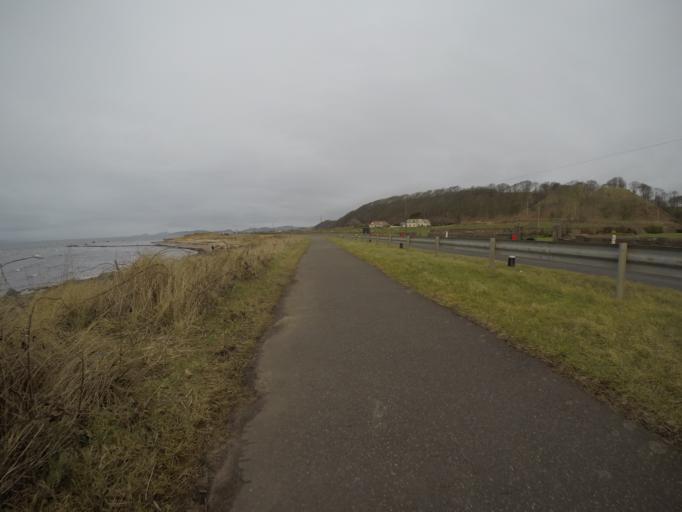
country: GB
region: Scotland
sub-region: North Ayrshire
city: West Kilbride
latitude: 55.6672
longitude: -4.8412
